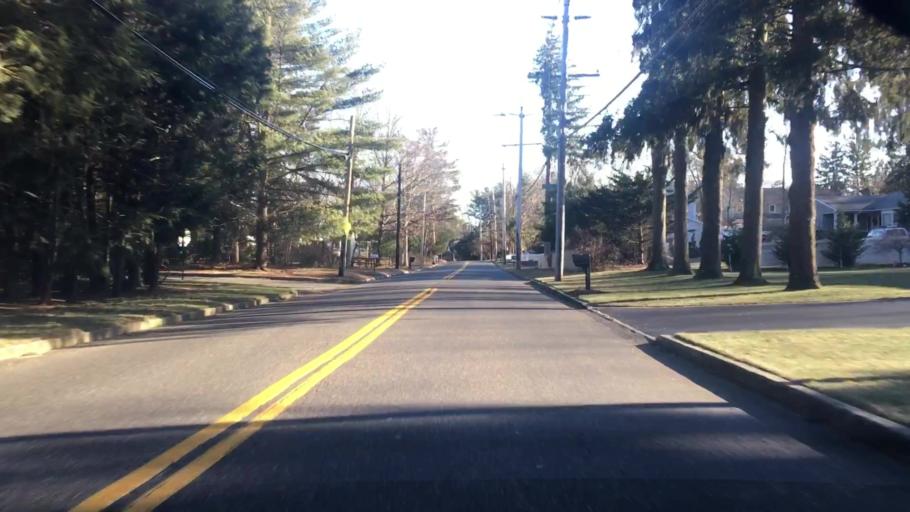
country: US
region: New York
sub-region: Suffolk County
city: Nesconset
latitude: 40.8492
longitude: -73.1445
